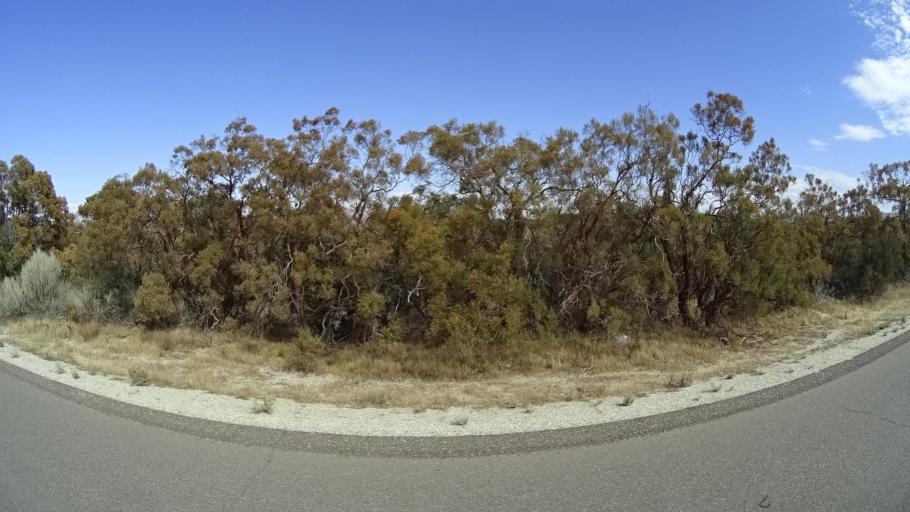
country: US
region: California
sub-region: San Diego County
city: Campo
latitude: 32.6853
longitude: -116.2937
